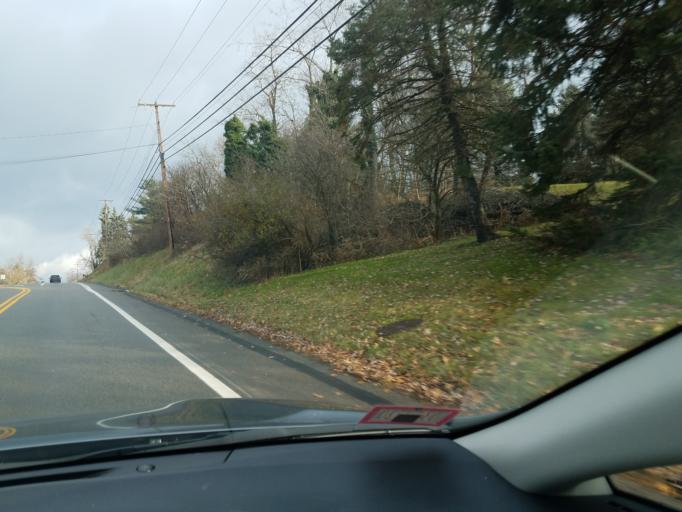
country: US
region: Pennsylvania
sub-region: Allegheny County
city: Franklin Park
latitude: 40.6077
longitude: -80.0996
